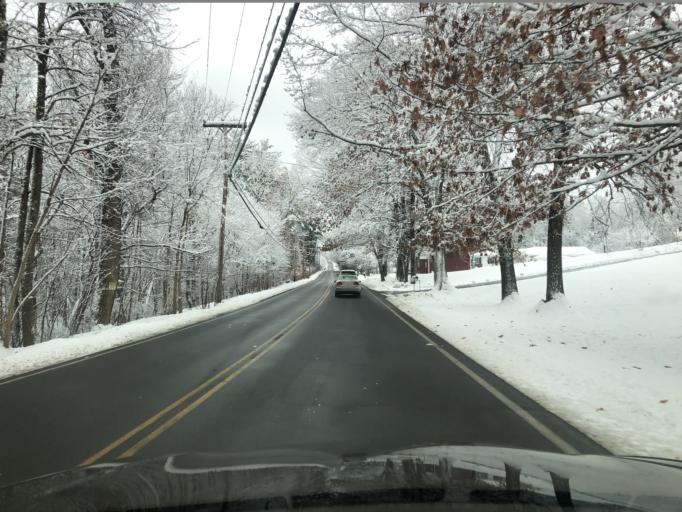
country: US
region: New Hampshire
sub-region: Strafford County
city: Somersworth
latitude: 43.2306
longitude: -70.8632
